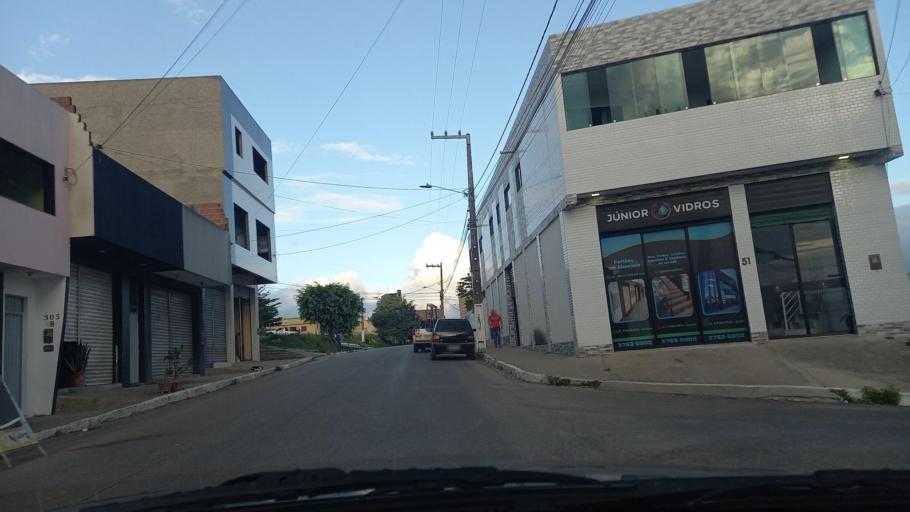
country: BR
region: Pernambuco
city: Garanhuns
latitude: -8.8881
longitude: -36.4611
